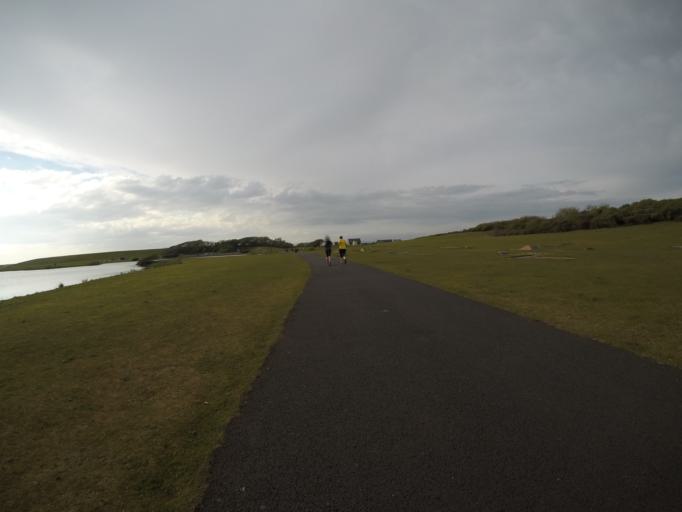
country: GB
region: Scotland
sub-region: North Ayrshire
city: Irvine
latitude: 55.6044
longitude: -4.6861
